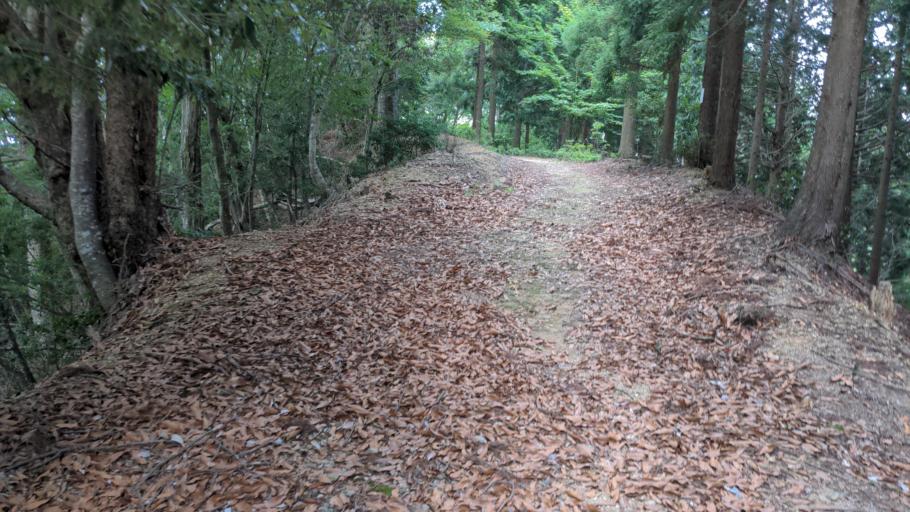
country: JP
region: Kyoto
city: Maizuru
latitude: 35.3941
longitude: 135.4415
